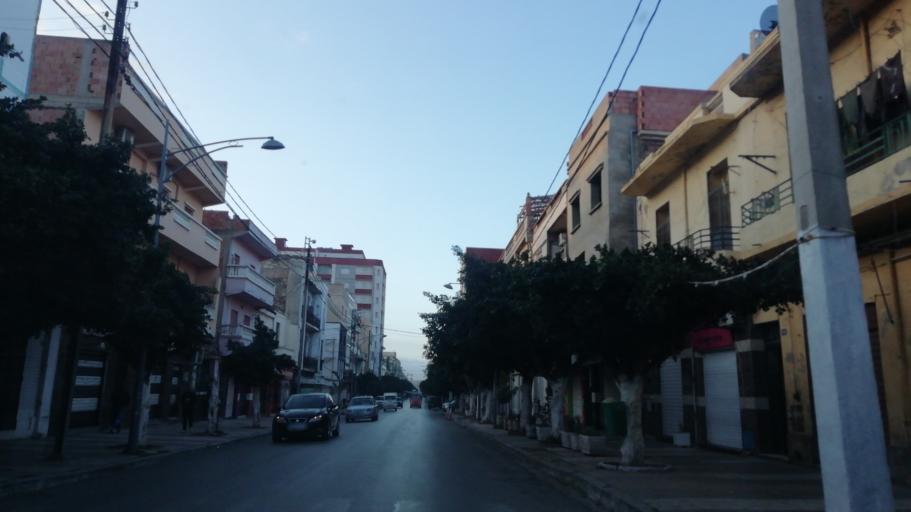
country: DZ
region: Oran
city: Oran
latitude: 35.6836
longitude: -0.6554
